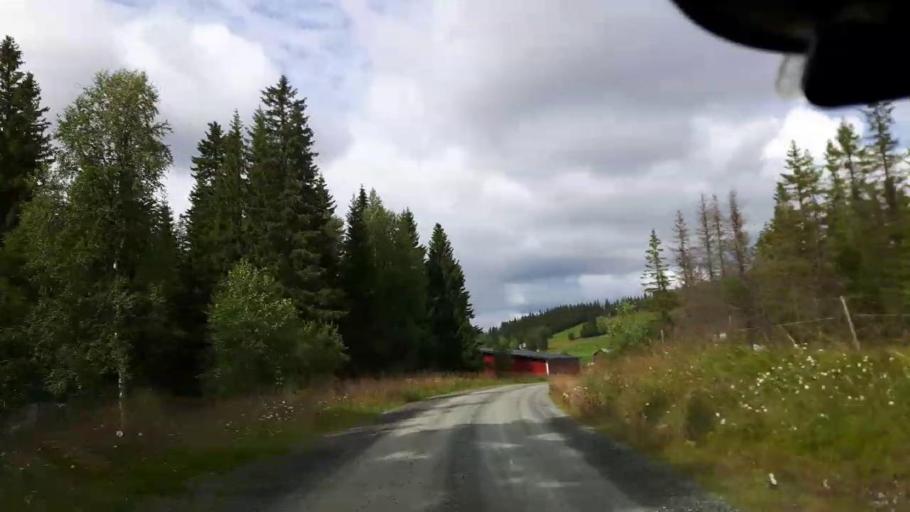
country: SE
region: Jaemtland
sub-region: Krokoms Kommun
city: Valla
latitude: 63.5762
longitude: 13.9047
